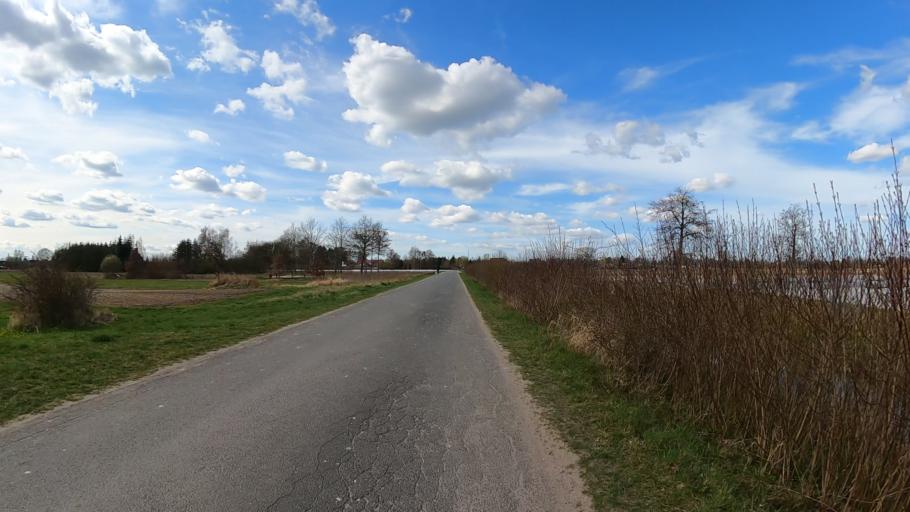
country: DE
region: Lower Saxony
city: Winsen
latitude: 53.4090
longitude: 10.1963
